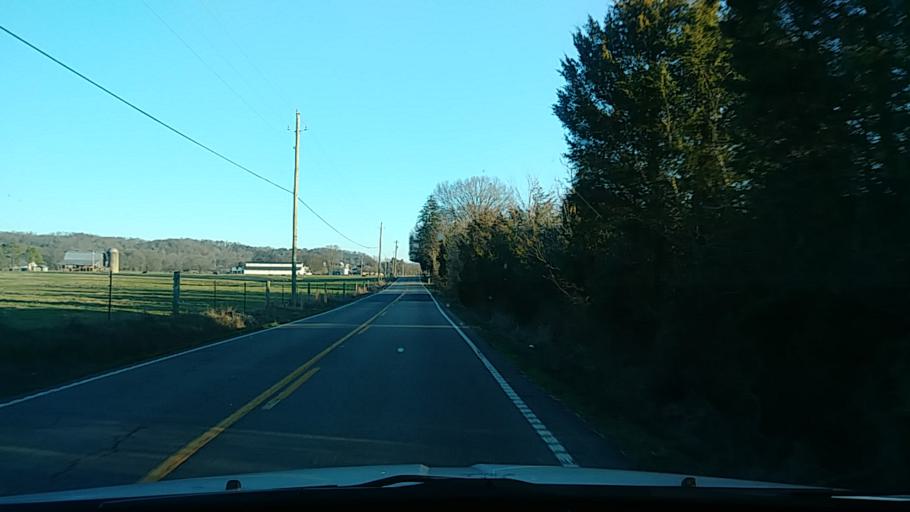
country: US
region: Tennessee
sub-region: Jefferson County
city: White Pine
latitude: 36.1406
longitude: -83.1413
